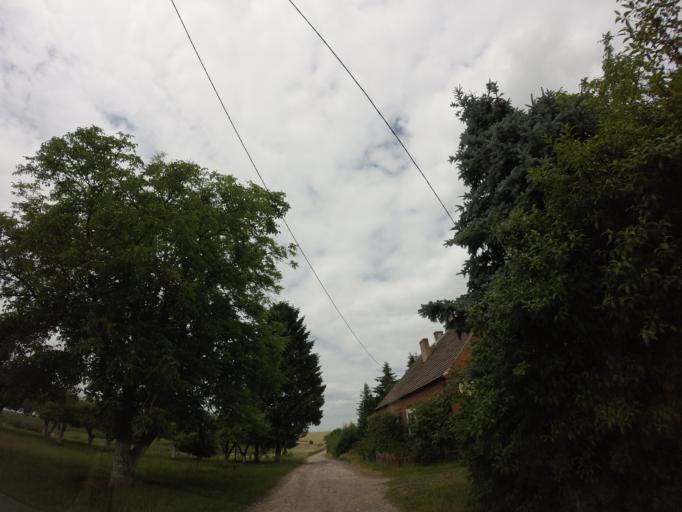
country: PL
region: West Pomeranian Voivodeship
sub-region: Powiat choszczenski
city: Krzecin
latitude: 53.0770
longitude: 15.5229
